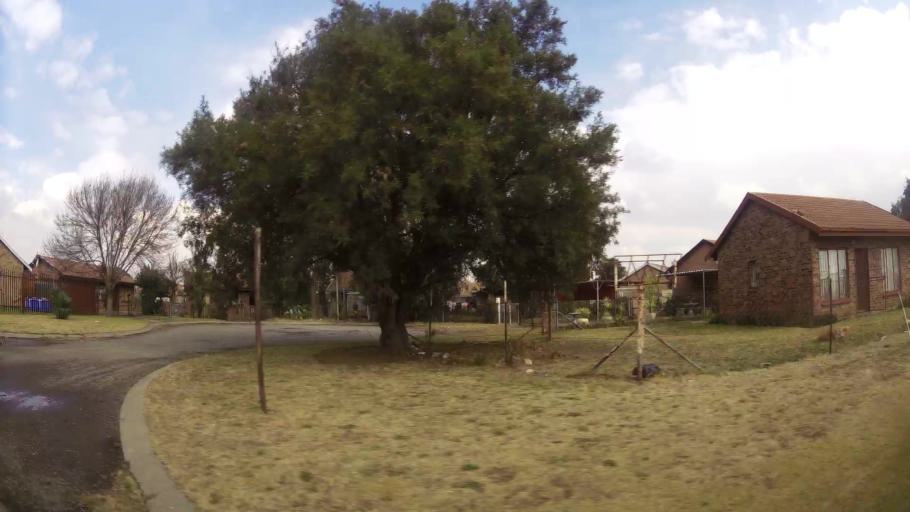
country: ZA
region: Gauteng
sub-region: Sedibeng District Municipality
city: Vereeniging
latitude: -26.6635
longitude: 27.9155
